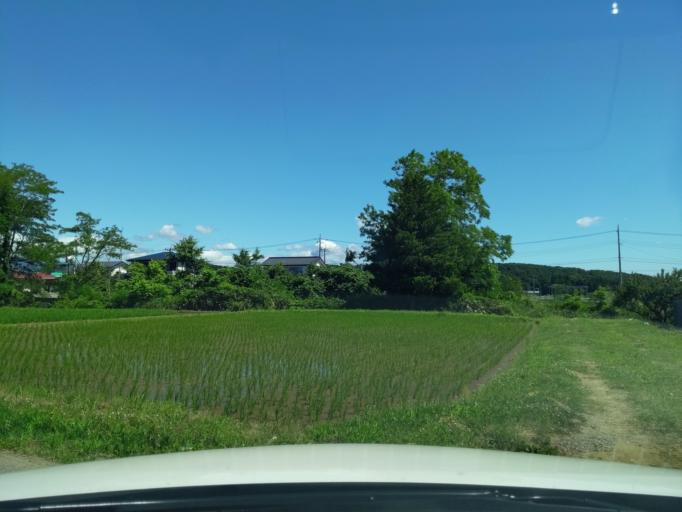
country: JP
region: Fukushima
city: Koriyama
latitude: 37.3874
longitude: 140.3045
